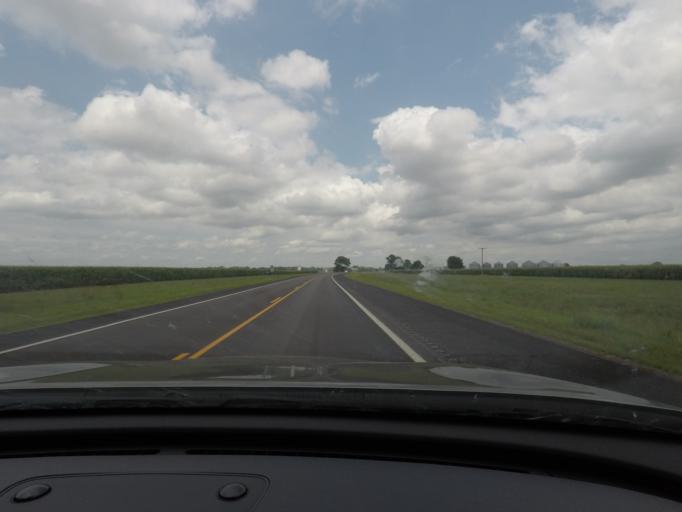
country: US
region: Missouri
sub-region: Carroll County
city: Carrollton
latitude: 39.3291
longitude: -93.4958
